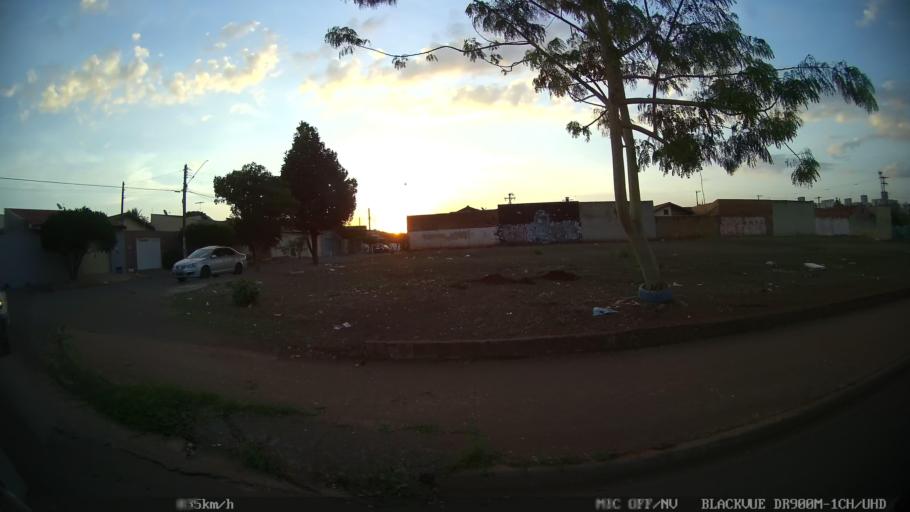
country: BR
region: Sao Paulo
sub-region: Ribeirao Preto
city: Ribeirao Preto
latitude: -21.1372
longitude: -47.8194
